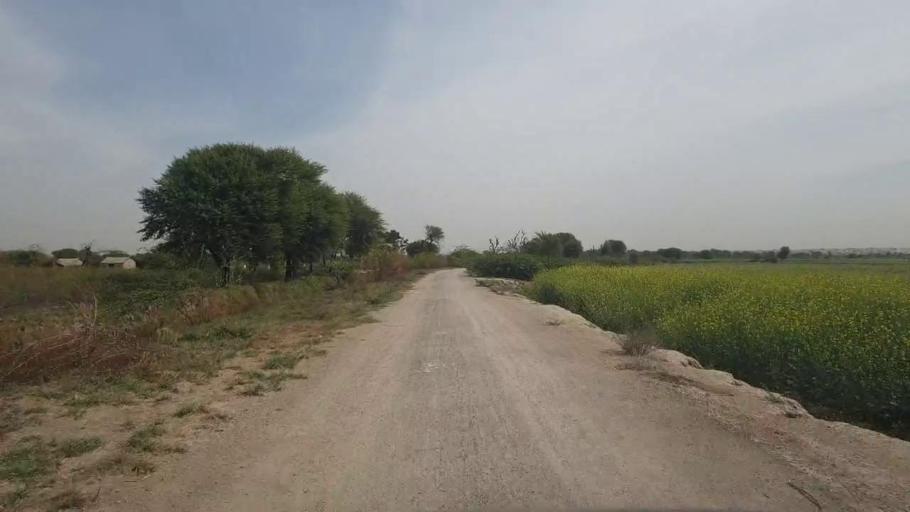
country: PK
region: Sindh
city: Umarkot
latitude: 25.2459
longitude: 69.7024
